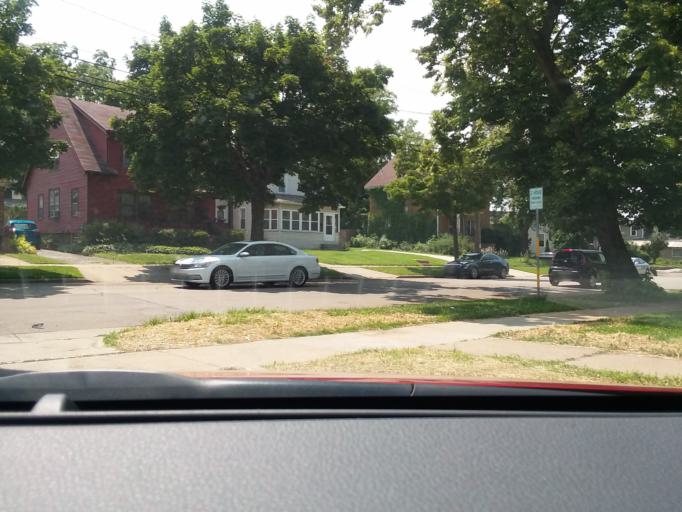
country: US
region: Wisconsin
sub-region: Dane County
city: Maple Bluff
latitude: 43.1001
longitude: -89.3459
